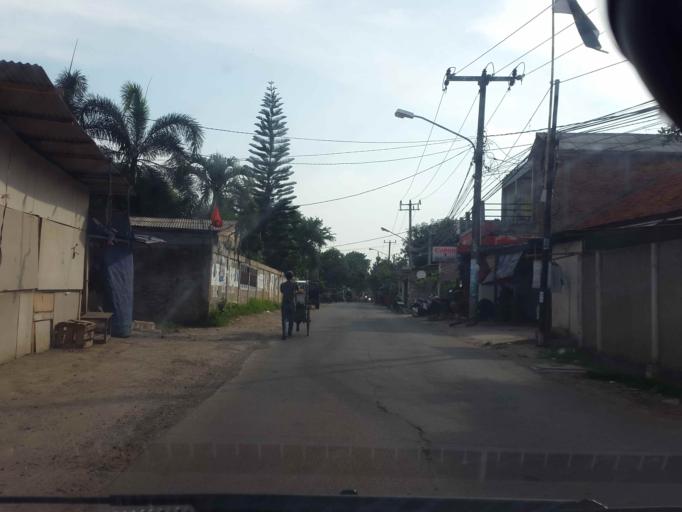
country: ID
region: West Java
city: Serpong
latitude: -6.2764
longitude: 106.6700
